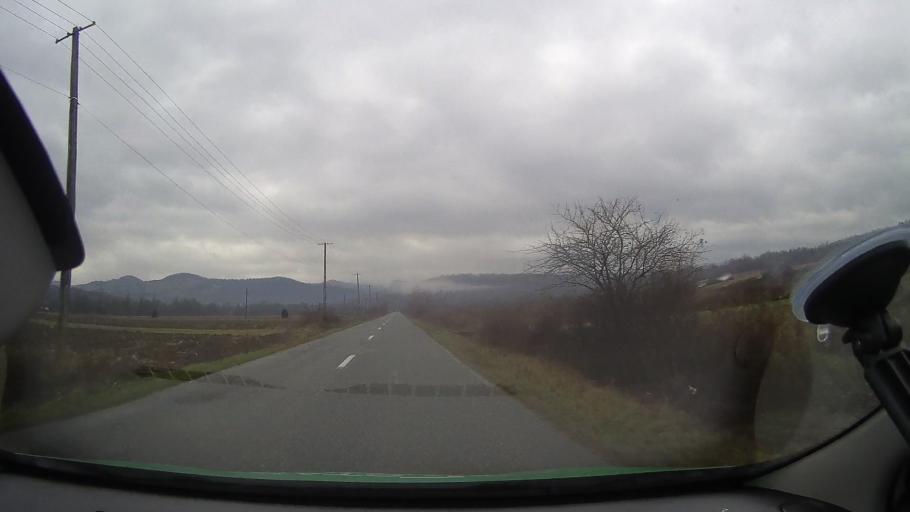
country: RO
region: Arad
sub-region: Comuna Brazii
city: Brazii
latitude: 46.2467
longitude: 22.3315
